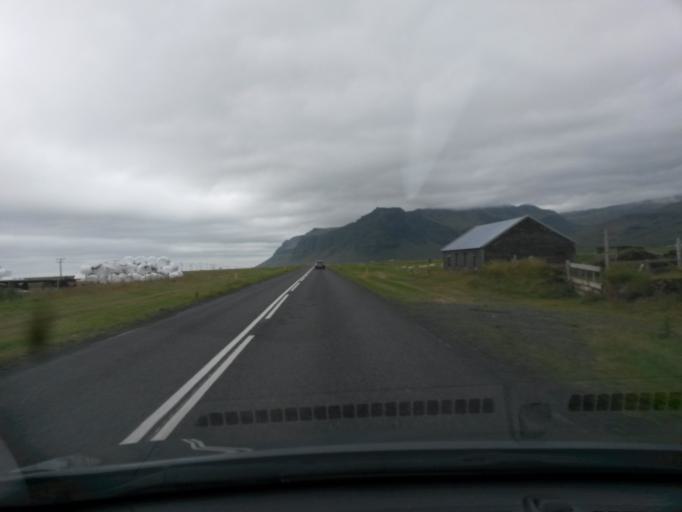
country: IS
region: South
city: Vestmannaeyjar
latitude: 63.5229
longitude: -19.5781
